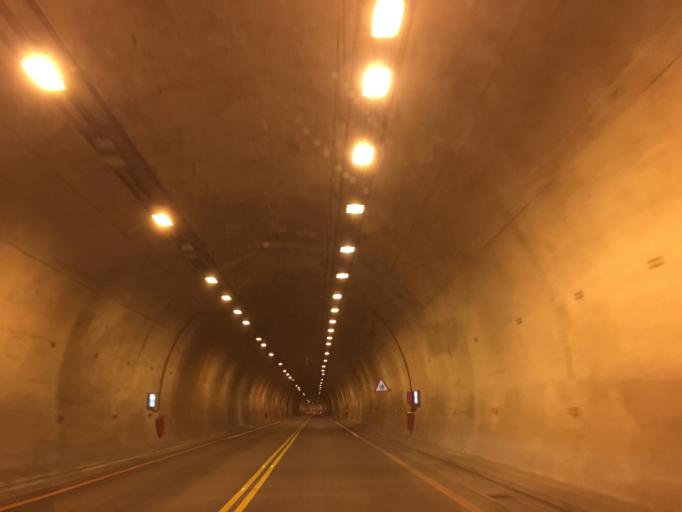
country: TW
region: Taiwan
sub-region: Hualien
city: Hualian
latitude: 24.1716
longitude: 121.5600
